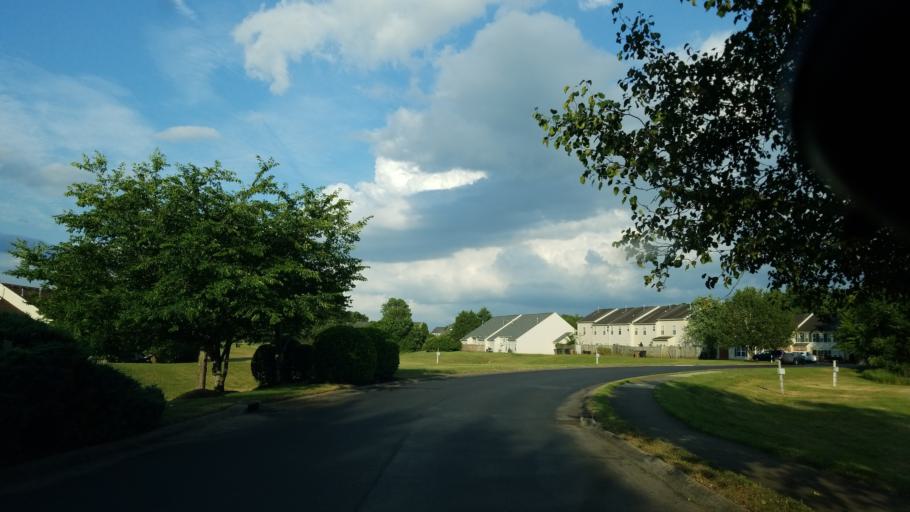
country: US
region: Tennessee
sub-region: Rutherford County
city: La Vergne
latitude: 36.0844
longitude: -86.6043
